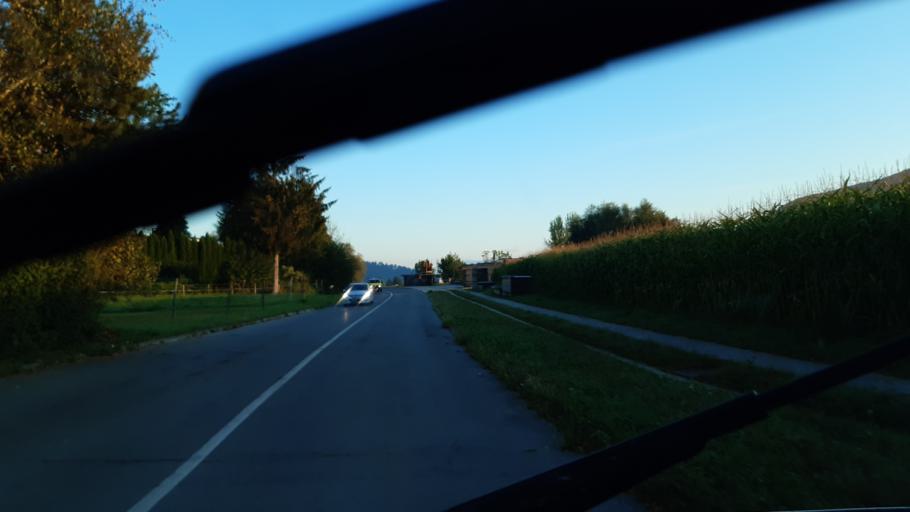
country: SI
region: Medvode
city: Zgornje Pirnice
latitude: 46.1042
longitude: 14.4443
